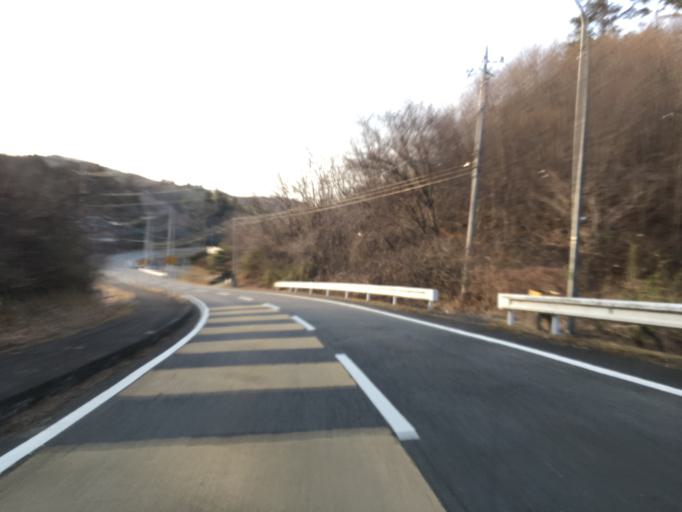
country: JP
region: Ibaraki
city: Daigo
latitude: 36.7898
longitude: 140.4158
